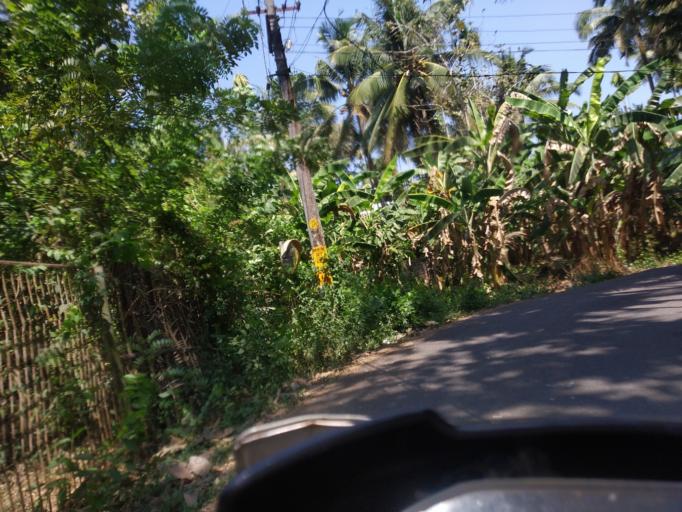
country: IN
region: Kerala
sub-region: Thrissur District
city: Kodungallur
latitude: 10.1796
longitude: 76.2147
